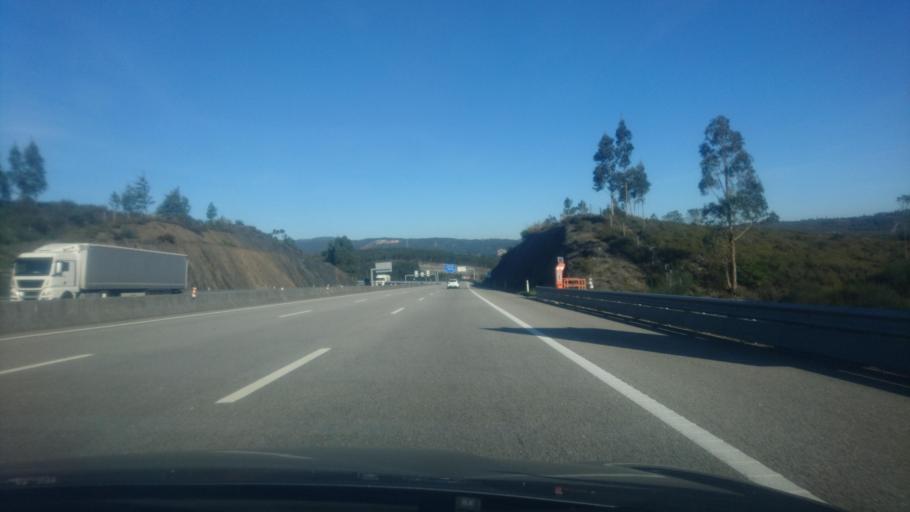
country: PT
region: Porto
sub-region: Paredes
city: Recarei
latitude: 41.1302
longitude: -8.4288
